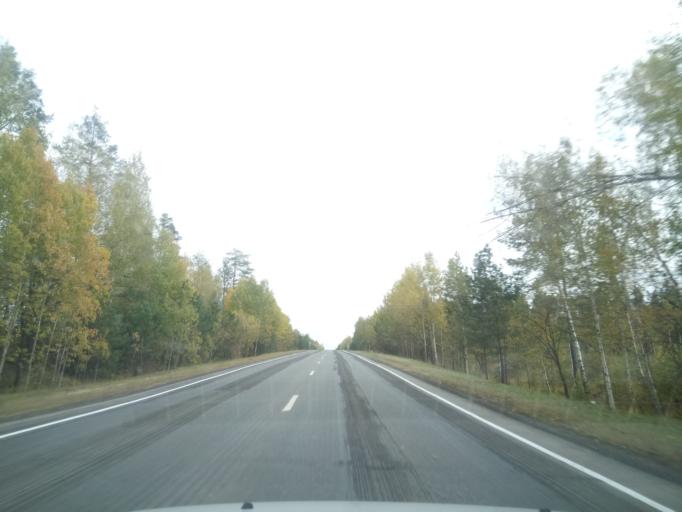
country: RU
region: Nizjnij Novgorod
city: Pochinki
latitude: 54.8250
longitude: 44.8348
